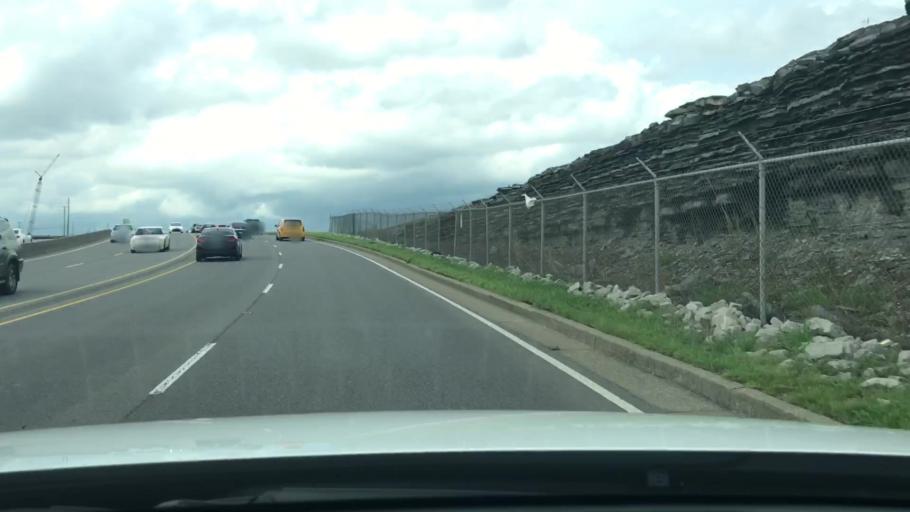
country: US
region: Tennessee
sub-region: Davidson County
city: Oak Hill
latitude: 36.1226
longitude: -86.6658
